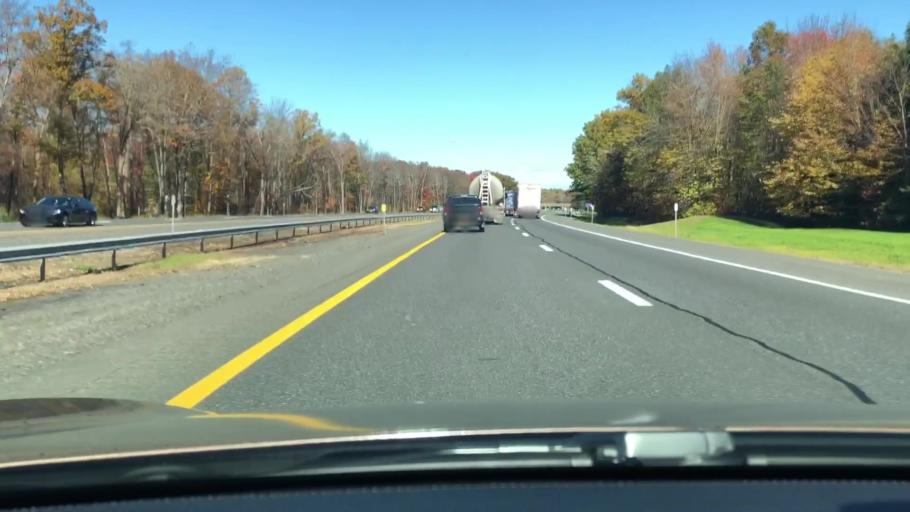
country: US
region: New York
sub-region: Ulster County
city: Clintondale
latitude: 41.7027
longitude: -74.0788
